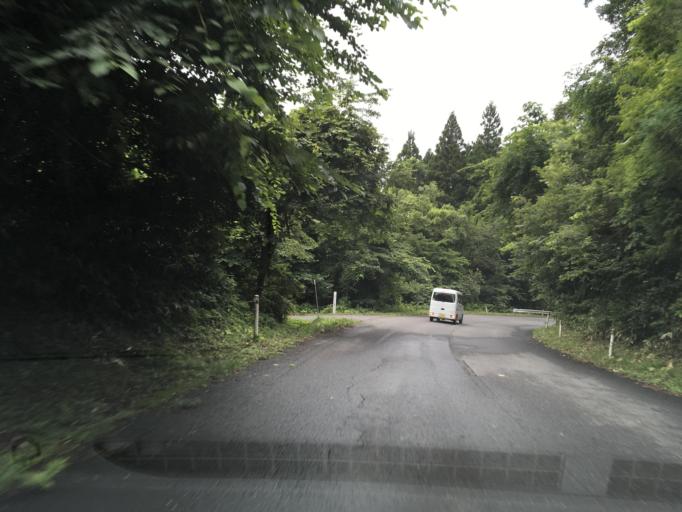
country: JP
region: Iwate
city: Ofunato
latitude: 38.8849
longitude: 141.4625
